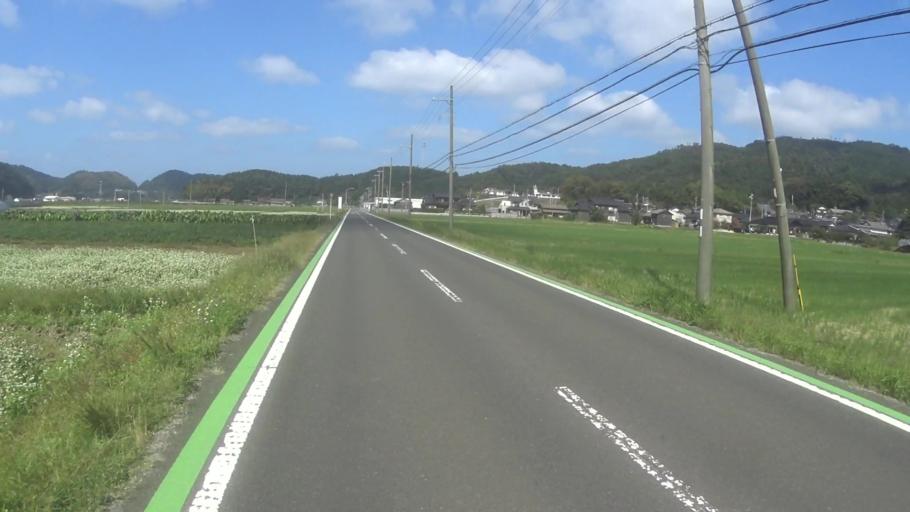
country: JP
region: Kyoto
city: Miyazu
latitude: 35.7202
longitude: 135.1079
